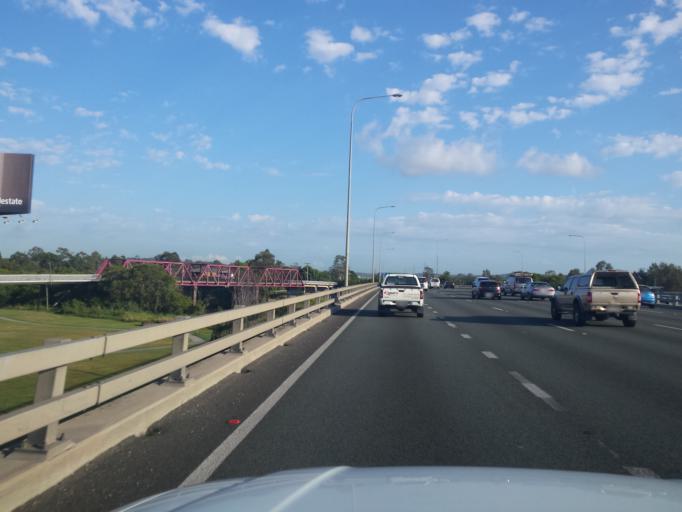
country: AU
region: Queensland
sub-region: Logan
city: Beenleigh
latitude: -27.6974
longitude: 153.1954
